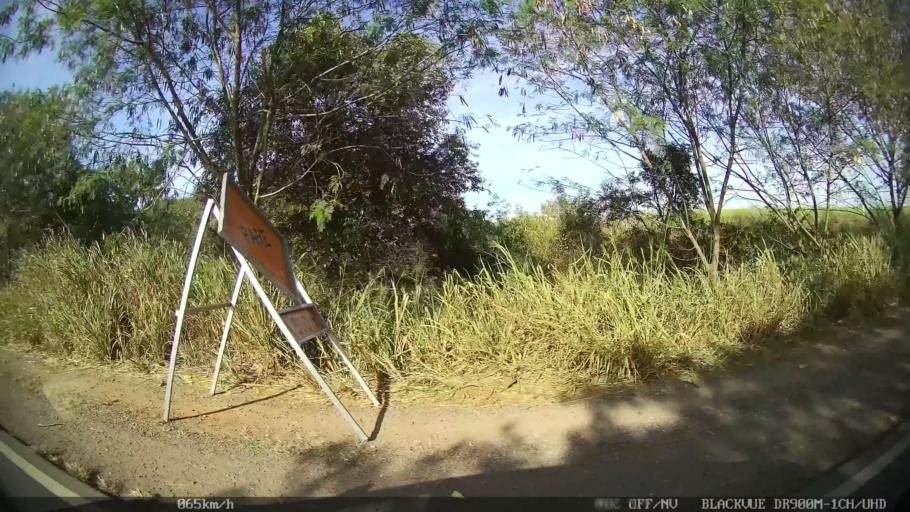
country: BR
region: Sao Paulo
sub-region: Rio Das Pedras
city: Rio das Pedras
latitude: -22.7918
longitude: -47.6250
